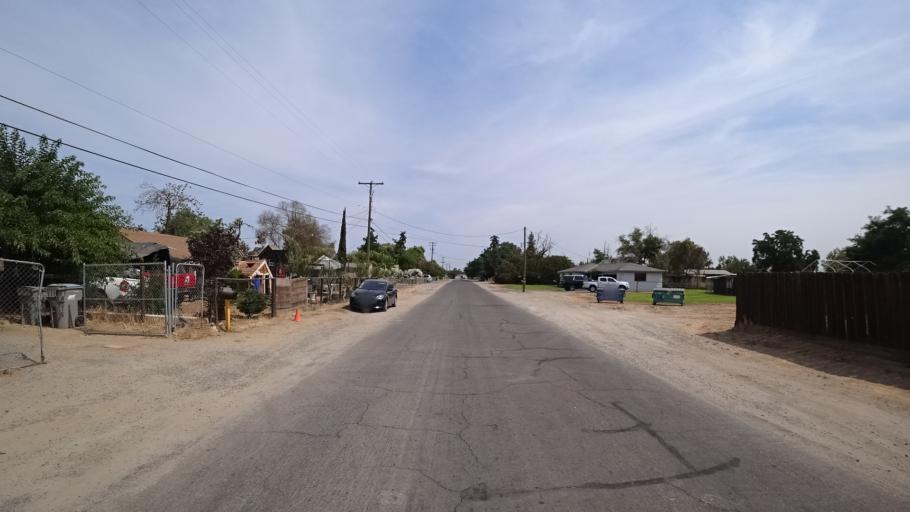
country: US
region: California
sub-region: Fresno County
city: West Park
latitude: 36.7578
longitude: -119.8747
